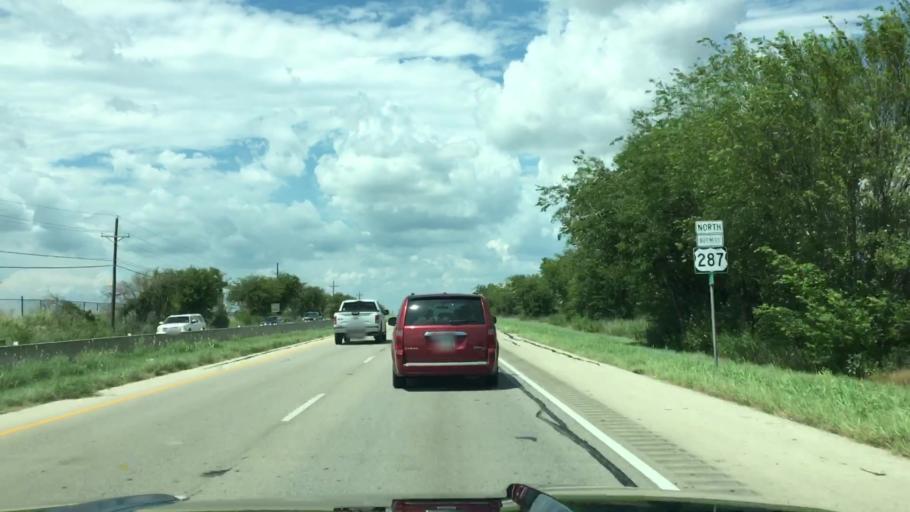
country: US
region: Texas
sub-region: Tarrant County
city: Saginaw
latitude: 32.8918
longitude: -97.3912
